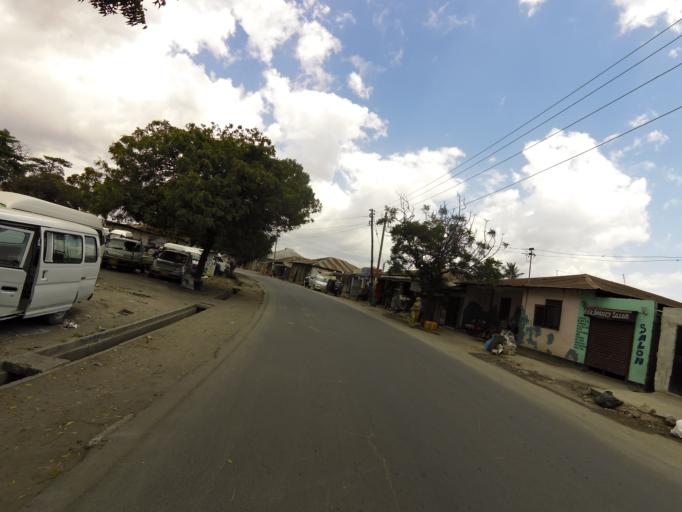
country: TZ
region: Dar es Salaam
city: Magomeni
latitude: -6.8004
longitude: 39.2538
